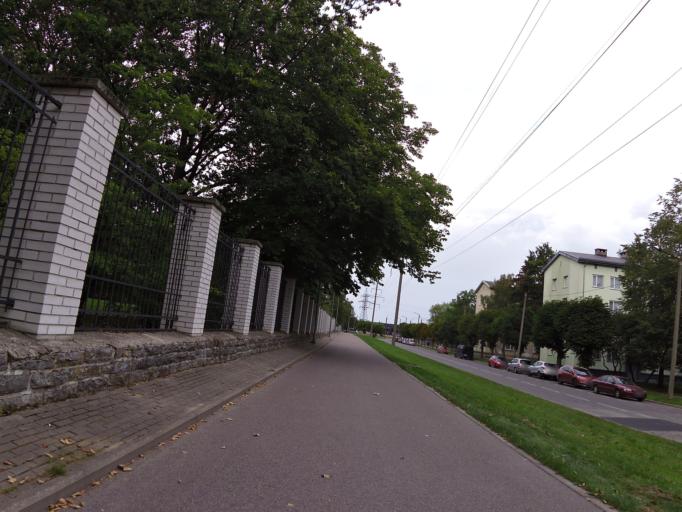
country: EE
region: Harju
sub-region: Tallinna linn
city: Tallinn
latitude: 59.4531
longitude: 24.6869
